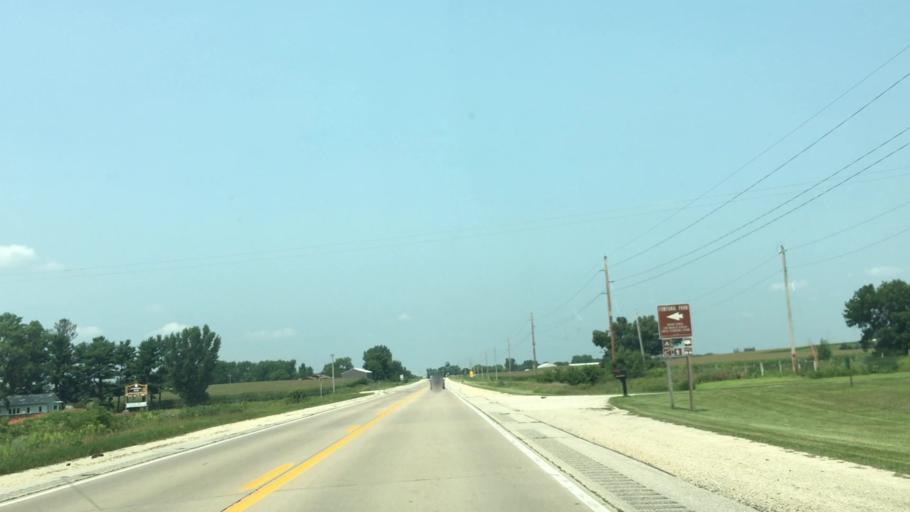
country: US
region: Iowa
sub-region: Fayette County
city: Oelwein
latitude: 42.6027
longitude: -91.9026
